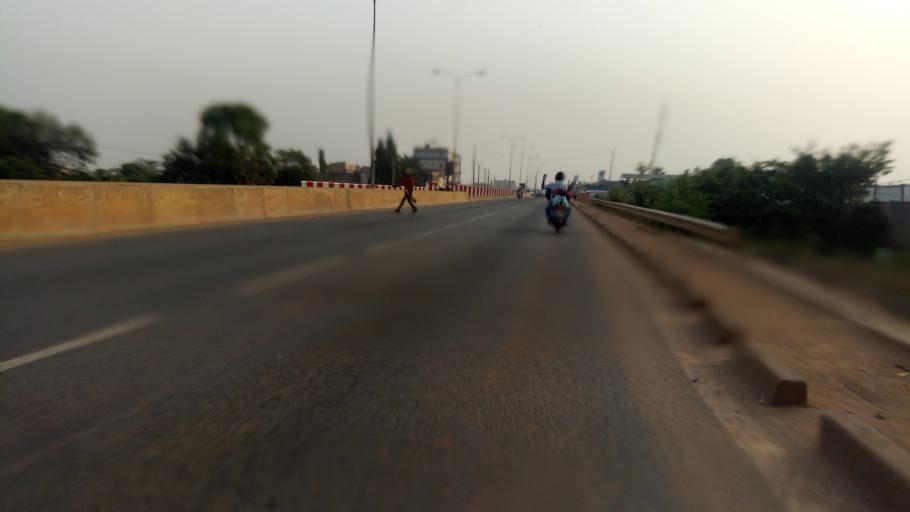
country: TG
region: Maritime
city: Tsevie
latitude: 6.2846
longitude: 1.2122
